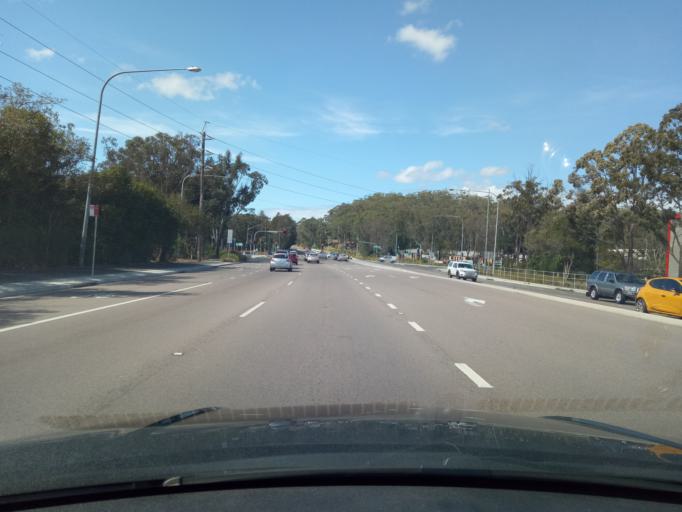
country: AU
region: New South Wales
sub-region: Wyong Shire
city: Chittaway Bay
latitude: -33.3269
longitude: 151.4281
